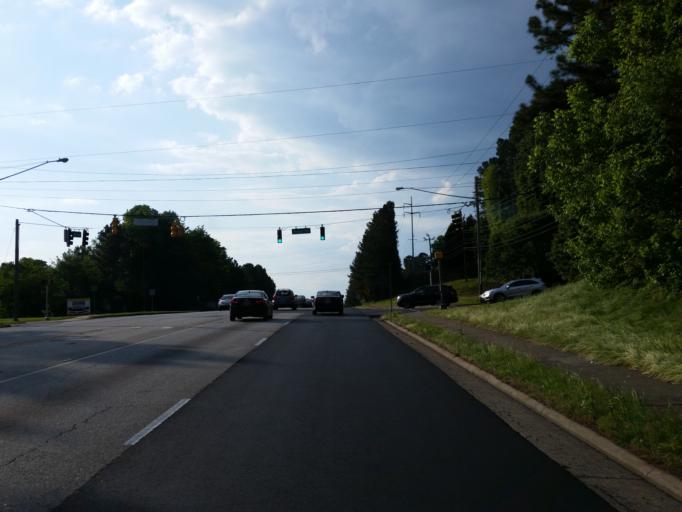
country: US
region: Georgia
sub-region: Cobb County
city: Smyrna
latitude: 33.8521
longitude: -84.5099
